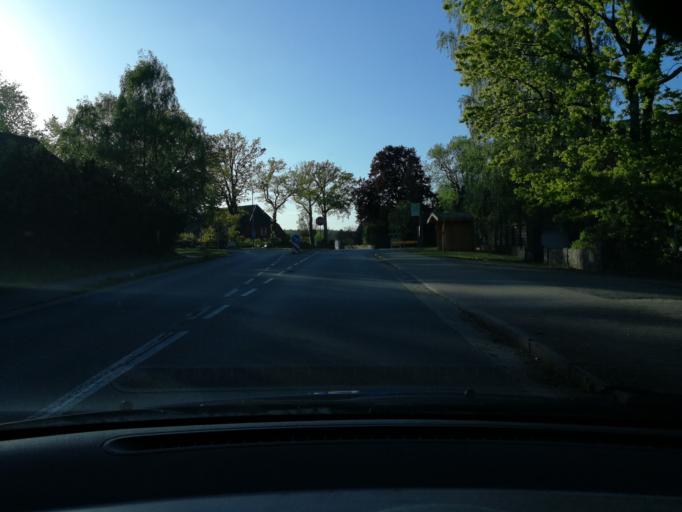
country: DE
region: Lower Saxony
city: Betzendorf
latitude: 53.1513
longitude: 10.2956
